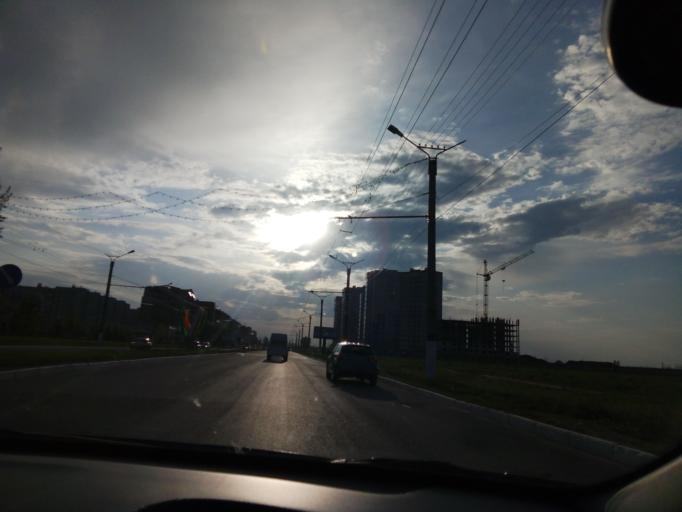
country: RU
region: Chuvashia
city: Novocheboksarsk
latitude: 56.1191
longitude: 47.4642
